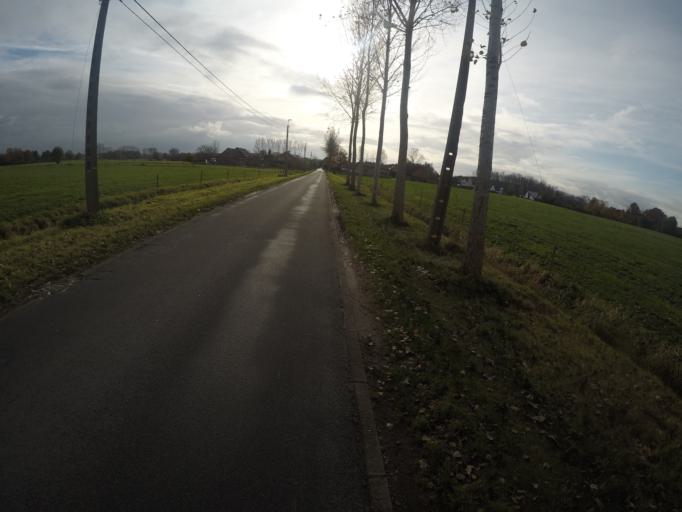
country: BE
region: Flanders
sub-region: Provincie Oost-Vlaanderen
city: Temse
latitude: 51.1622
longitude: 4.1902
